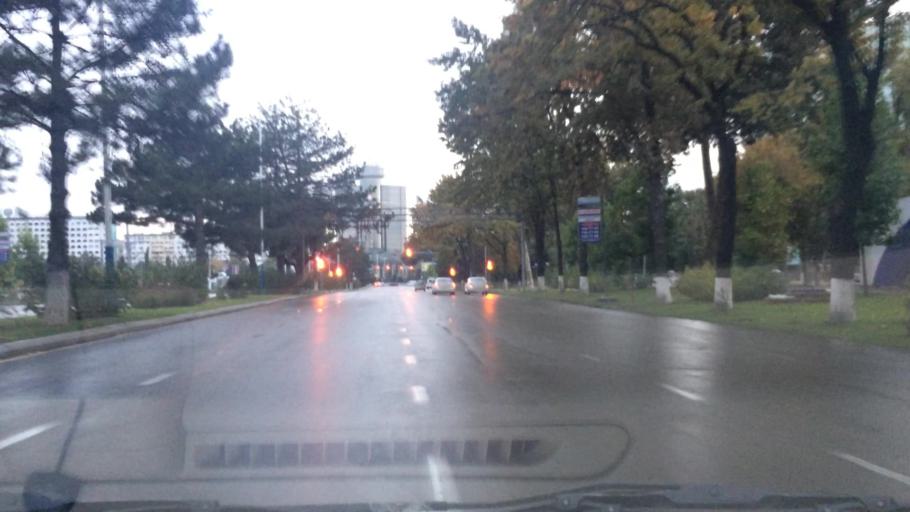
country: UZ
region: Toshkent Shahri
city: Tashkent
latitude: 41.3118
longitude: 69.2445
